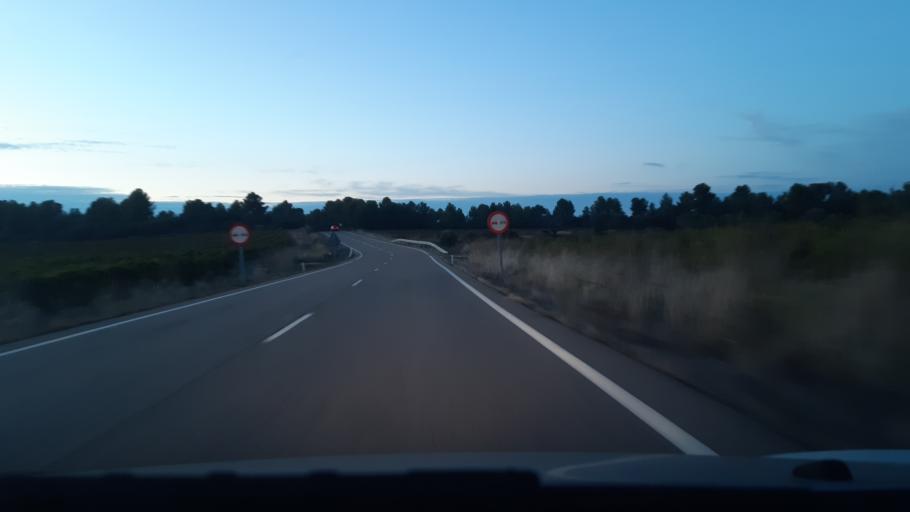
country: ES
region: Aragon
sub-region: Provincia de Teruel
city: Calaceite
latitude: 40.9605
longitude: 0.2138
